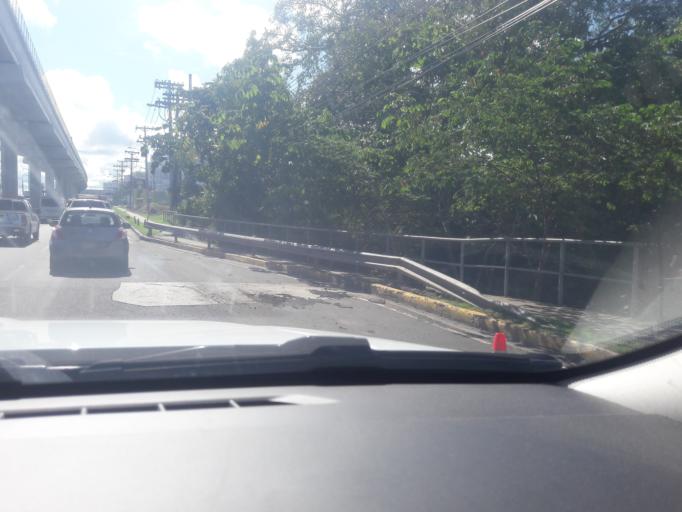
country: PA
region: Panama
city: San Miguelito
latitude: 9.0486
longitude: -79.4611
